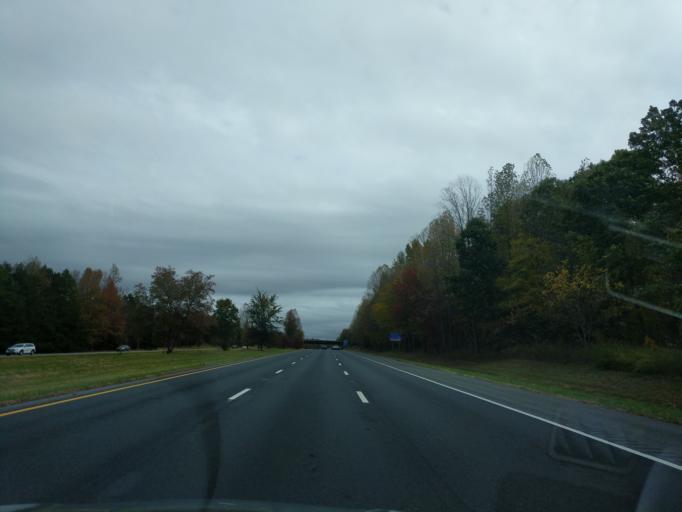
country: US
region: North Carolina
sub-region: Davidson County
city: Lexington
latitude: 35.7766
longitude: -80.2847
